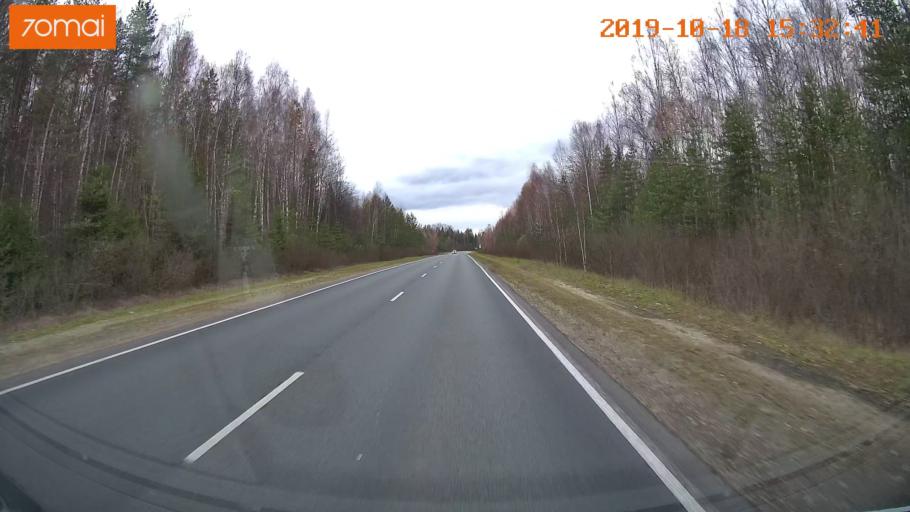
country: RU
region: Vladimir
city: Anopino
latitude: 55.8295
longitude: 40.6492
